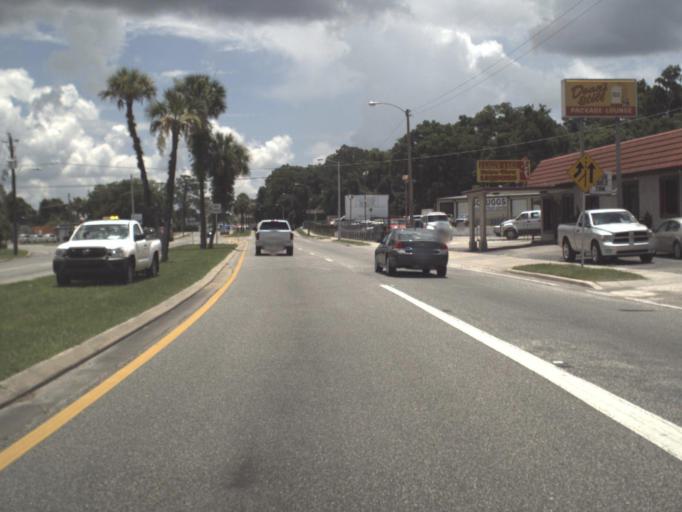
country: US
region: Florida
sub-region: Putnam County
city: Palatka
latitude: 29.6537
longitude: -81.6551
